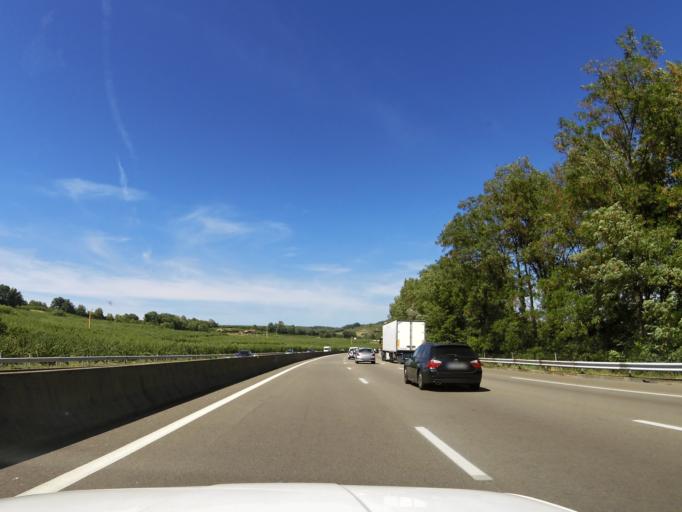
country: FR
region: Rhone-Alpes
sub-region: Departement de la Drome
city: Mercurol
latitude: 45.0952
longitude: 4.8786
